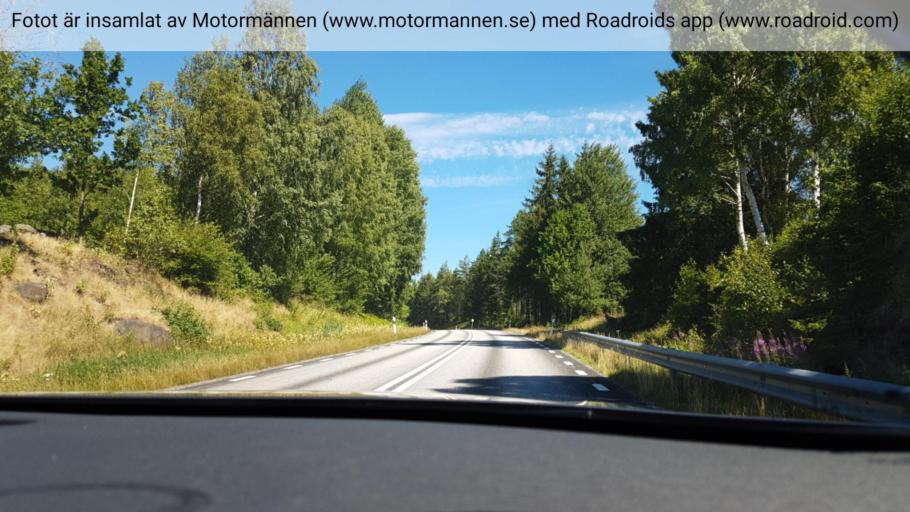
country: SE
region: Joenkoeping
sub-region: Gnosjo Kommun
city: Hillerstorp
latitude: 57.3297
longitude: 13.8070
